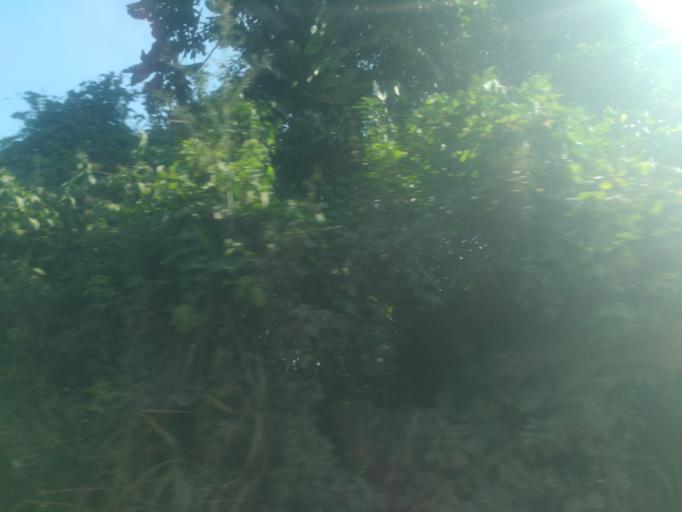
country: NG
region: Ogun
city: Abeokuta
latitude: 7.1403
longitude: 3.2553
